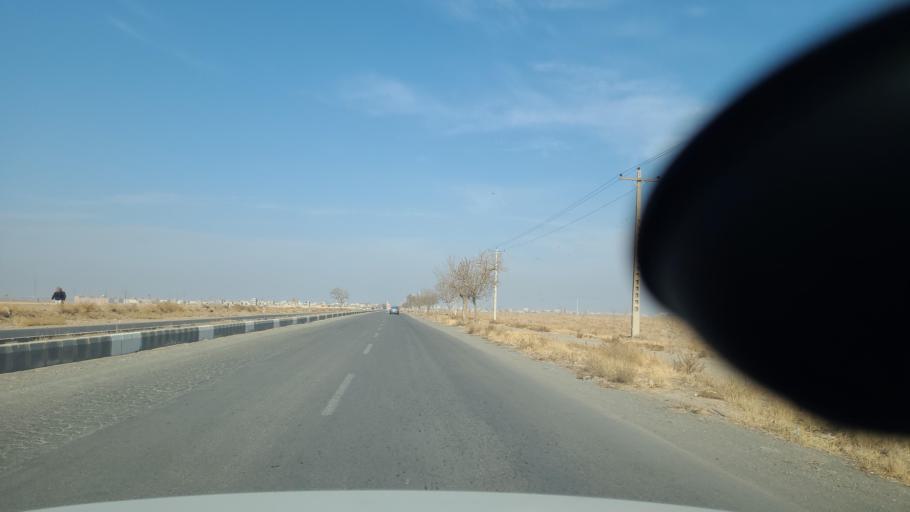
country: IR
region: Razavi Khorasan
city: Fariman
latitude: 35.6700
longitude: 59.8421
